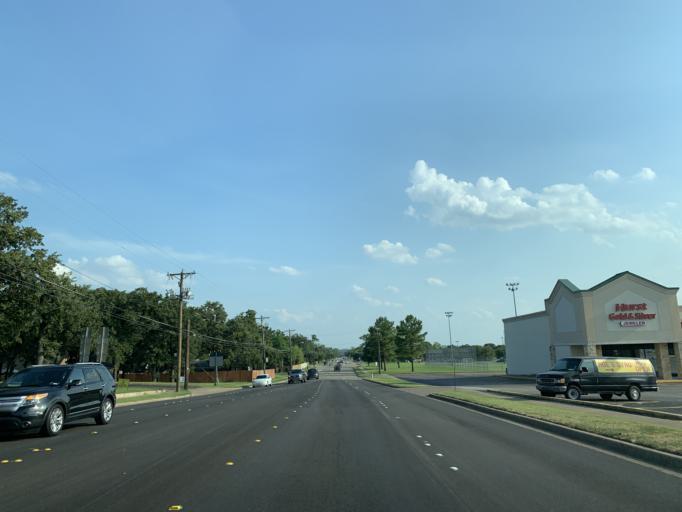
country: US
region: Texas
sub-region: Tarrant County
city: Hurst
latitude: 32.8232
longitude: -97.1865
